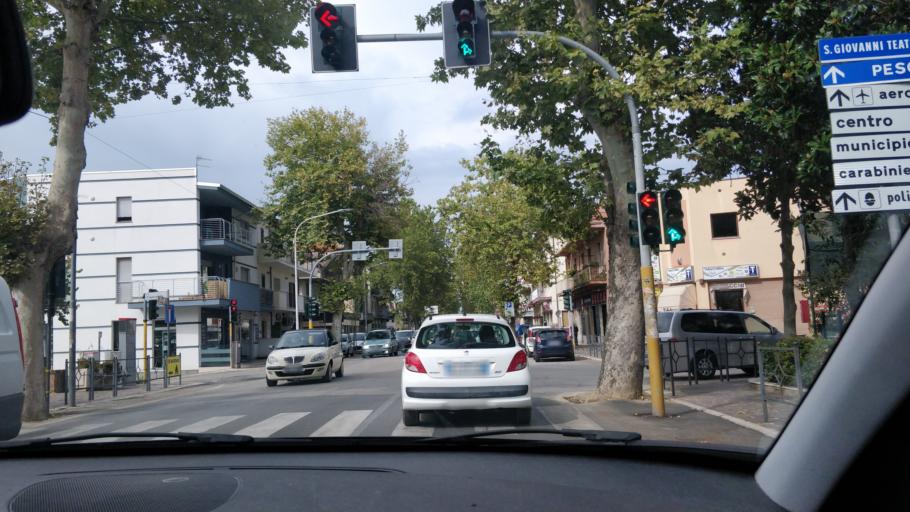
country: IT
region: Abruzzo
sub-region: Provincia di Chieti
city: Sambuceto
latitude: 42.4247
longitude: 14.1850
